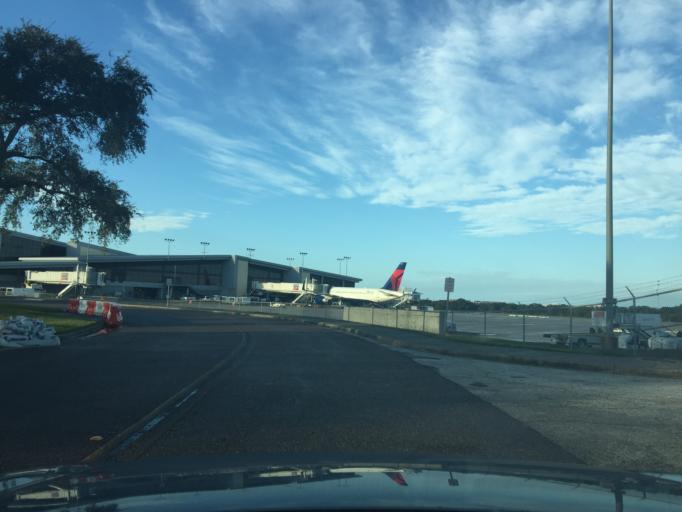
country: US
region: Florida
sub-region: Hillsborough County
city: Egypt Lake-Leto
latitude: 27.9820
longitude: -82.5365
